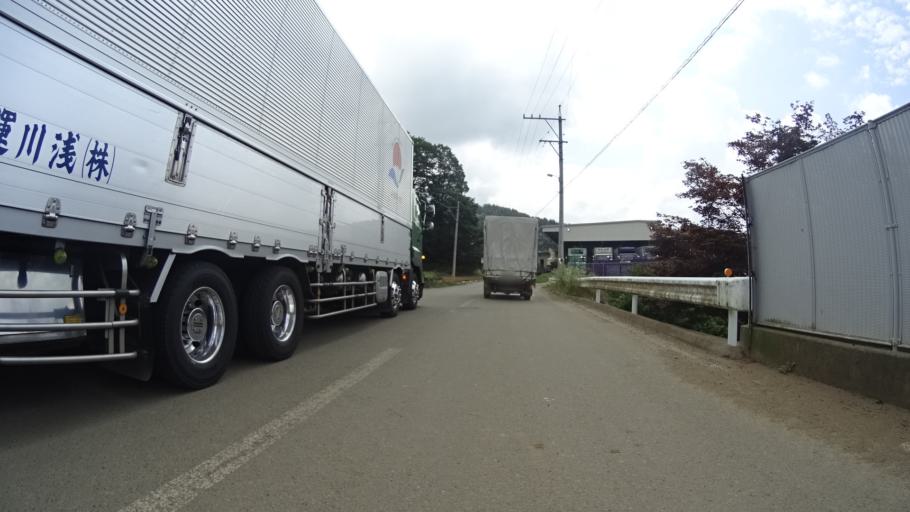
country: JP
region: Yamanashi
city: Nirasaki
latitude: 35.9128
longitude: 138.4538
